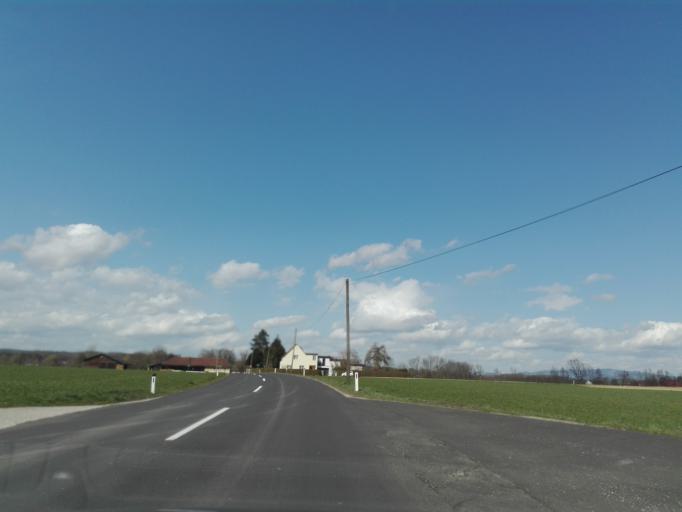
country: AT
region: Upper Austria
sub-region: Wels-Land
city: Holzhausen
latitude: 48.2177
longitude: 14.1284
